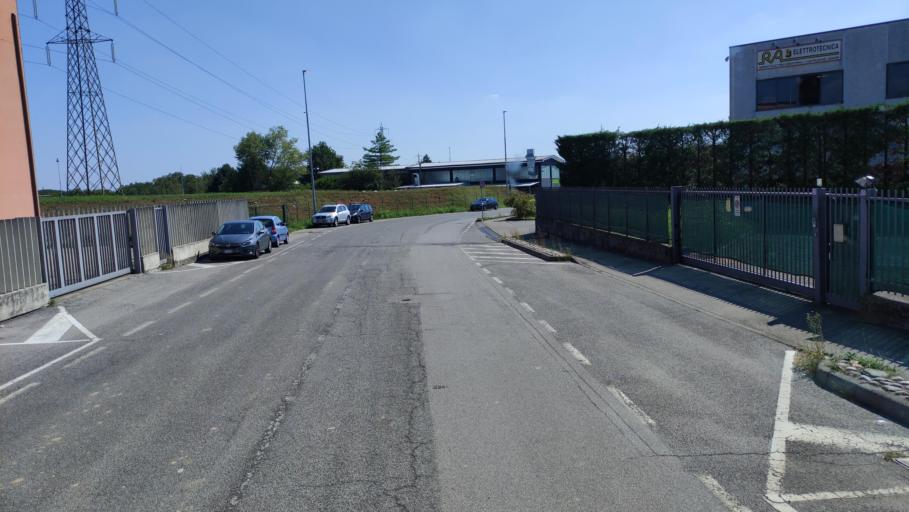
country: IT
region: Lombardy
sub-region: Provincia di Monza e Brianza
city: Mezzago
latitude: 45.6127
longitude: 9.4400
